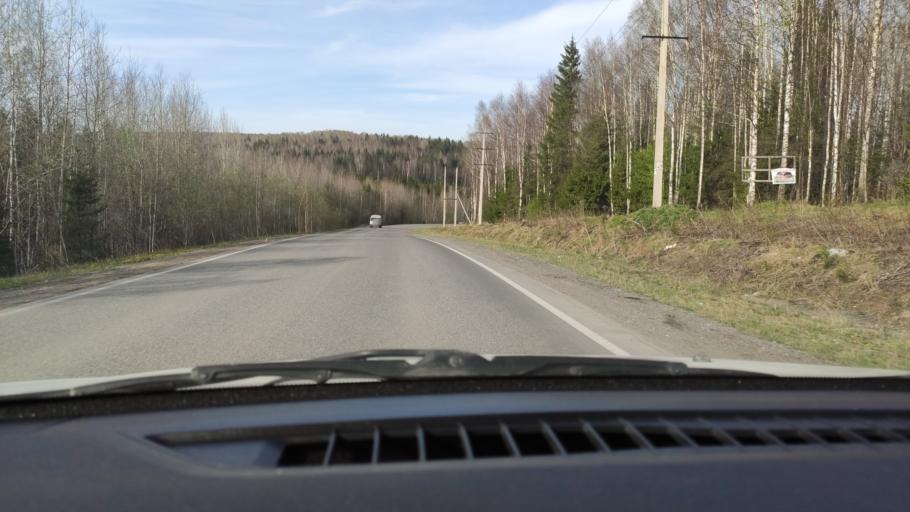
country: RU
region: Perm
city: Novyye Lyady
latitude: 57.9571
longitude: 56.5349
